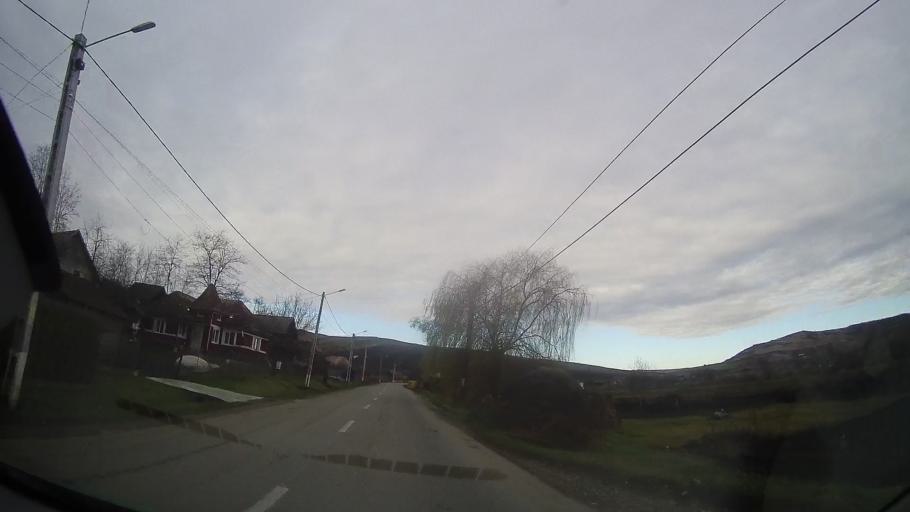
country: RO
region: Cluj
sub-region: Comuna Camarasu
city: Camarasu
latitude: 46.8171
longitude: 24.1379
